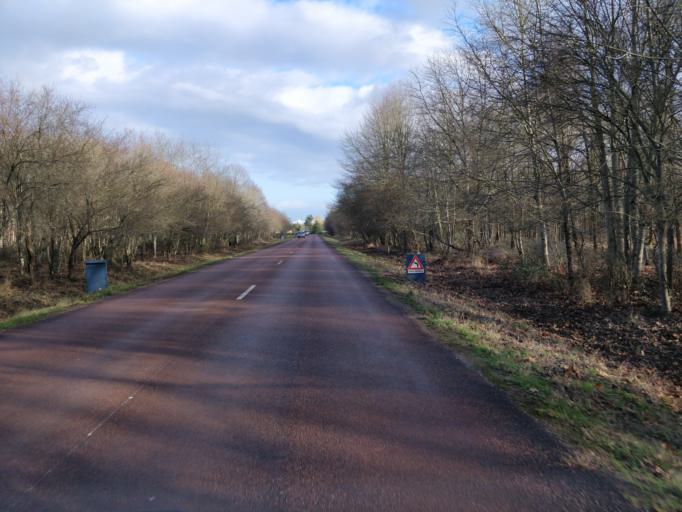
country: FR
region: Centre
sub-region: Departement du Loir-et-Cher
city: Muides-sur-Loire
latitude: 47.6543
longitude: 1.5325
